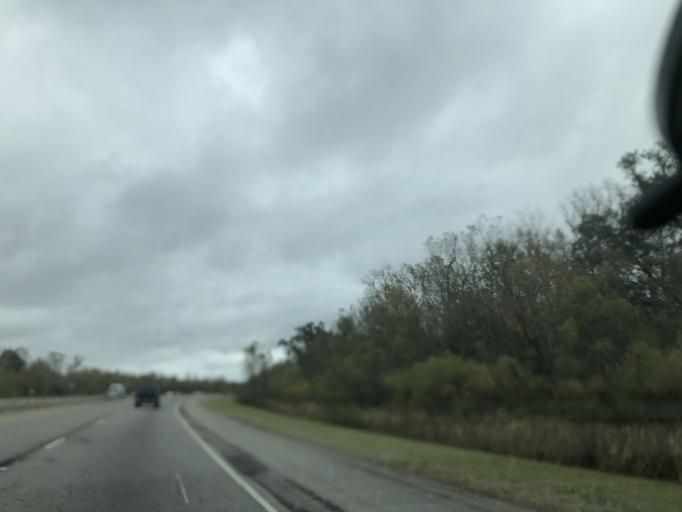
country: US
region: Louisiana
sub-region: Saint Charles Parish
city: Destrehan
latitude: 29.9612
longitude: -90.3620
